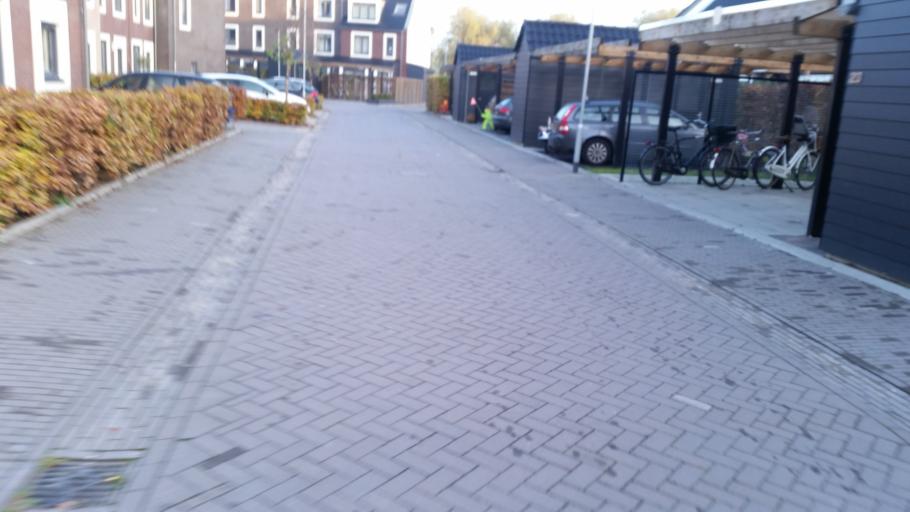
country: NL
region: North Holland
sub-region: Gemeente Ouder-Amstel
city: Ouderkerk aan de Amstel
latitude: 52.2921
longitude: 4.9043
